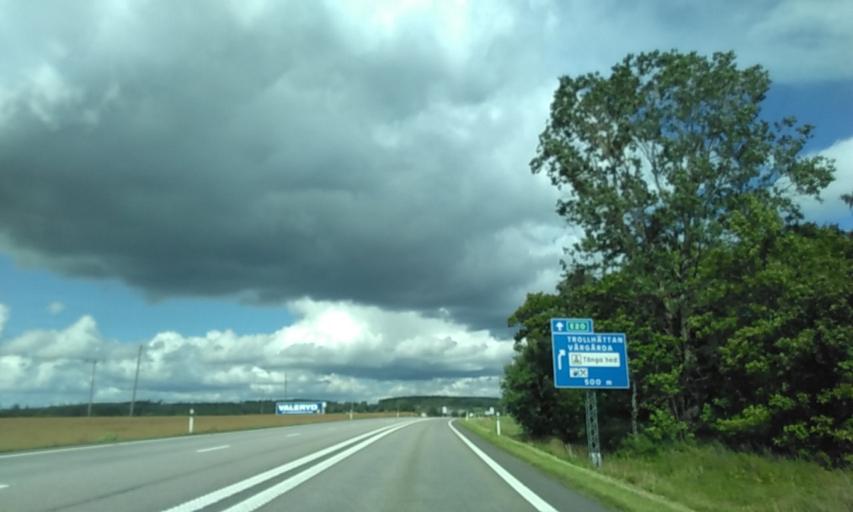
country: SE
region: Vaestra Goetaland
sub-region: Vargarda Kommun
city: Vargarda
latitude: 58.0358
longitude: 12.7890
